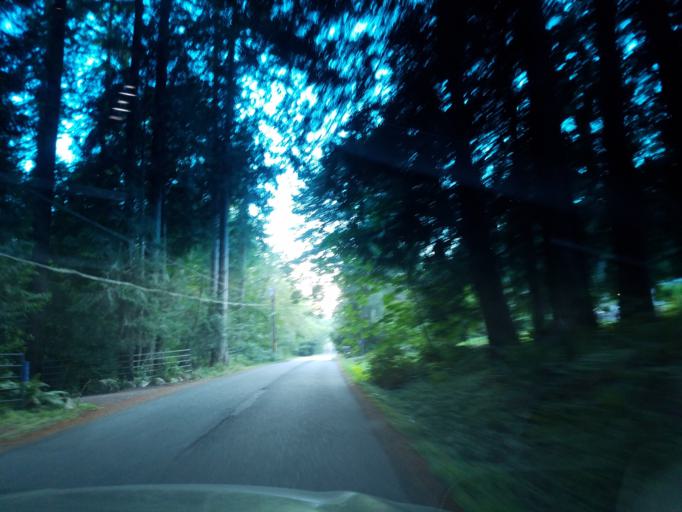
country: US
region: Washington
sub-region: King County
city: Ames Lake
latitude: 47.6444
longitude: -121.9833
